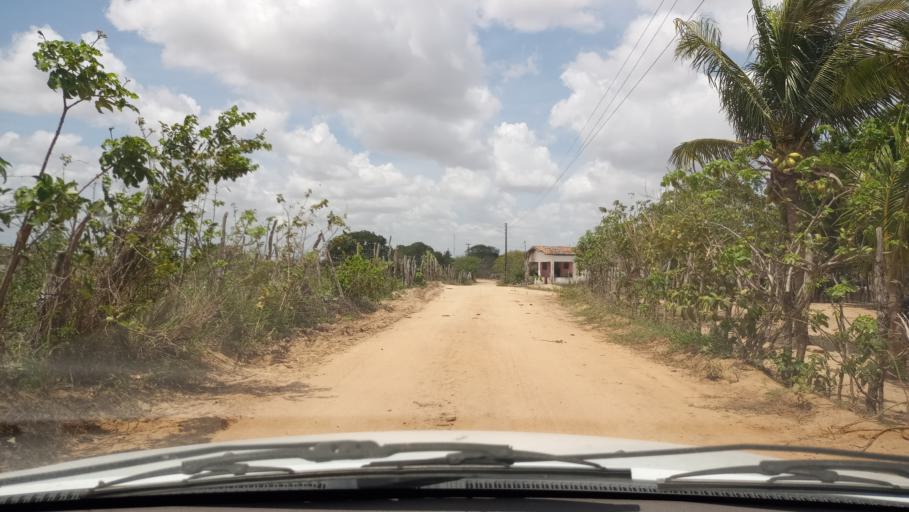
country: BR
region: Rio Grande do Norte
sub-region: Brejinho
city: Brejinho
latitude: -6.2693
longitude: -35.3440
